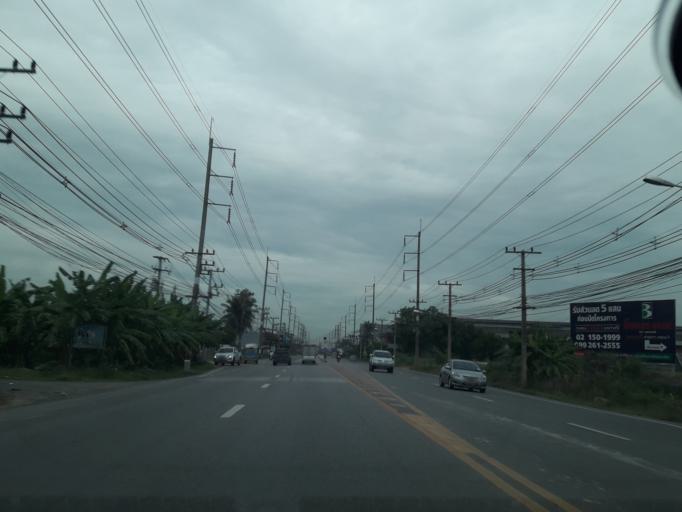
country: TH
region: Pathum Thani
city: Ban Lam Luk Ka
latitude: 13.9472
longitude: 100.7852
